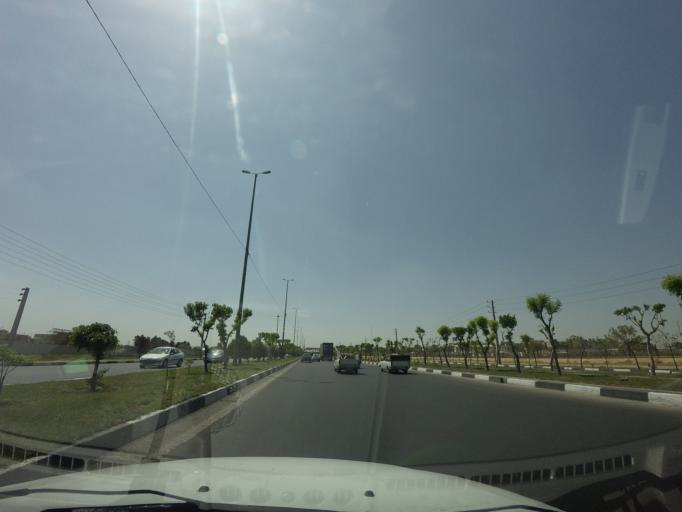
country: IR
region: Tehran
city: Eslamshahr
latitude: 35.5738
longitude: 51.2645
